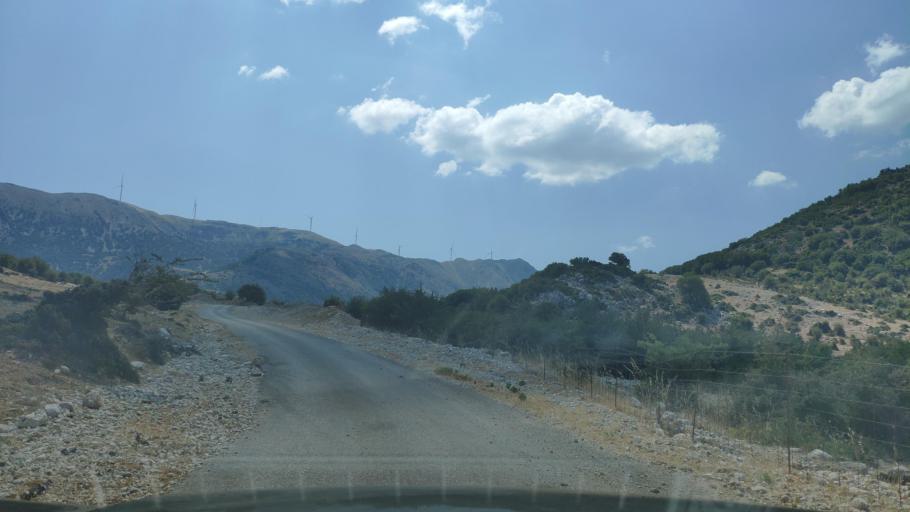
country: GR
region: West Greece
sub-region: Nomos Aitolias kai Akarnanias
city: Monastirakion
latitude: 38.7960
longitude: 20.9564
